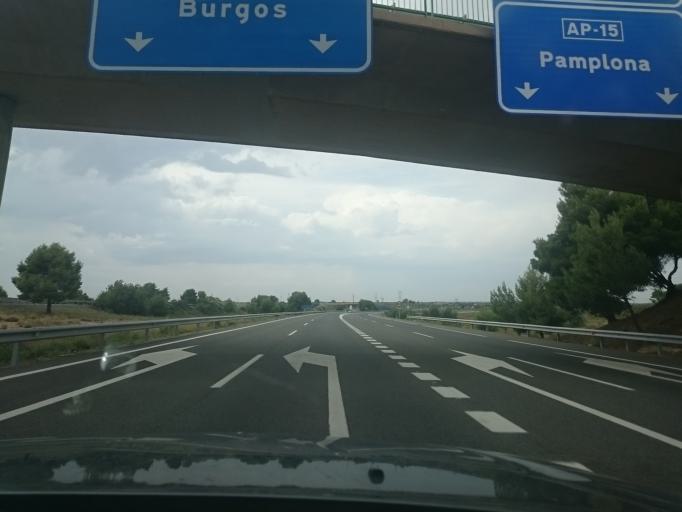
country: ES
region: Navarre
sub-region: Provincia de Navarra
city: Corella
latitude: 42.0914
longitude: -1.7187
